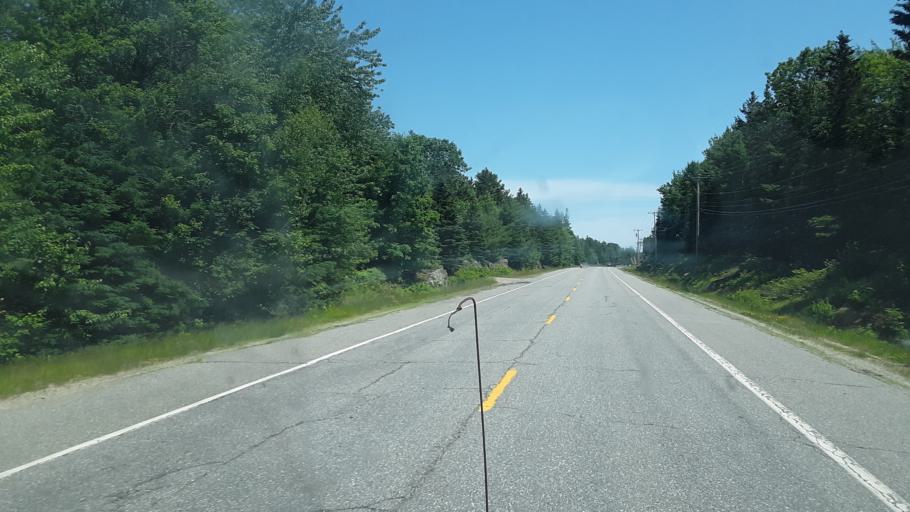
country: US
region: Maine
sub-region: Washington County
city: Steuben
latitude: 44.5112
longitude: -67.9555
